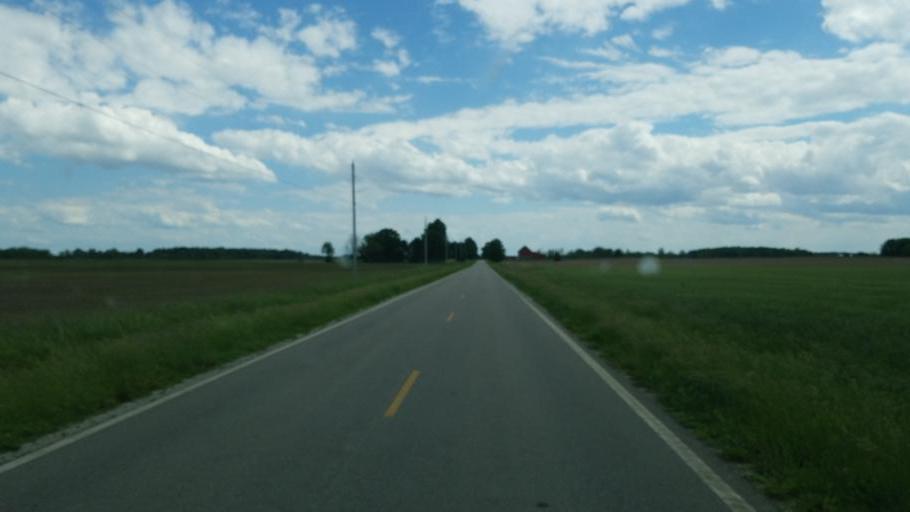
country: US
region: Ohio
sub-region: Huron County
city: Plymouth
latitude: 41.0878
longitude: -82.6111
